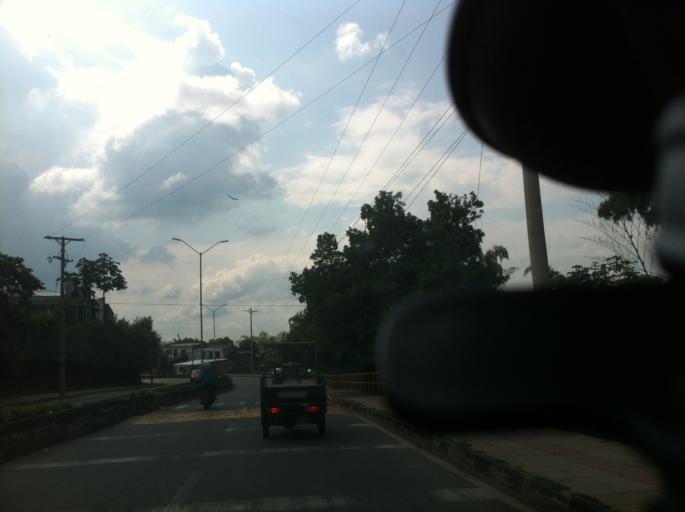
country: CO
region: Quindio
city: Armenia
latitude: 4.5187
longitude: -75.7021
